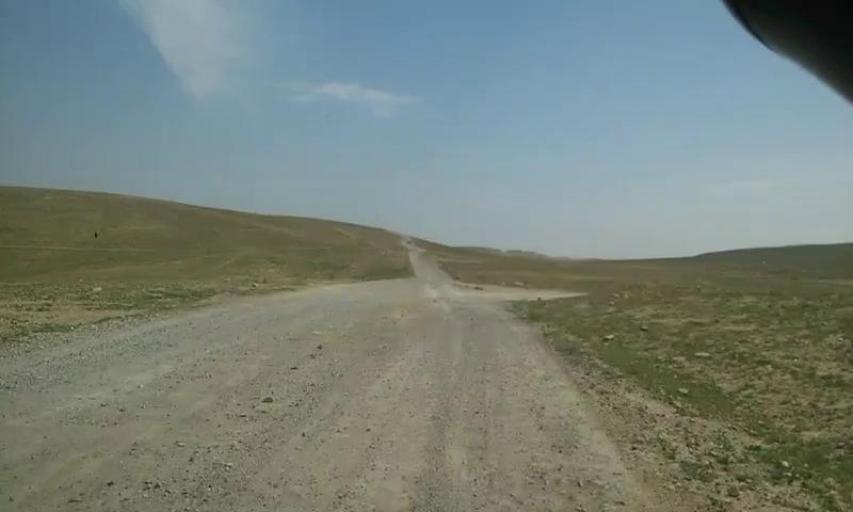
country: PS
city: `Arab ar Rashaydah
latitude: 31.5251
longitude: 35.2959
